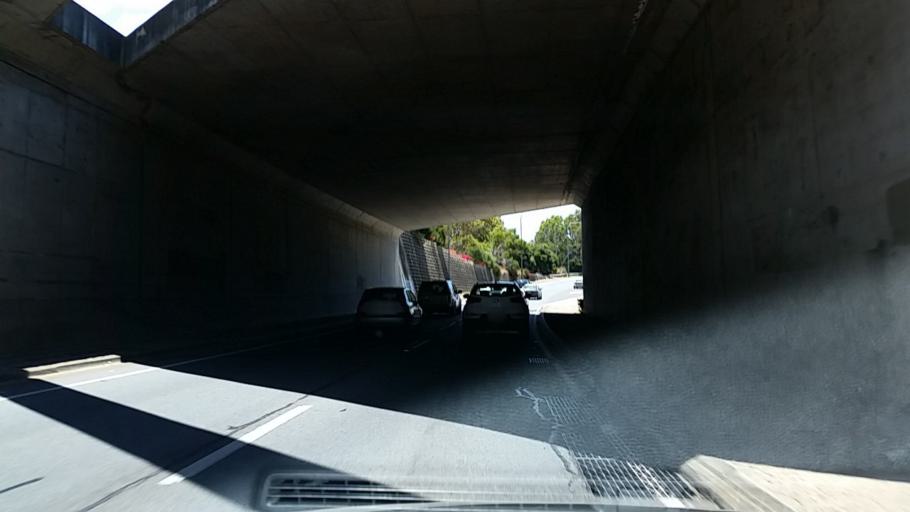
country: AU
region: South Australia
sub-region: Salisbury
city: Salisbury
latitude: -34.7602
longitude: 138.6422
